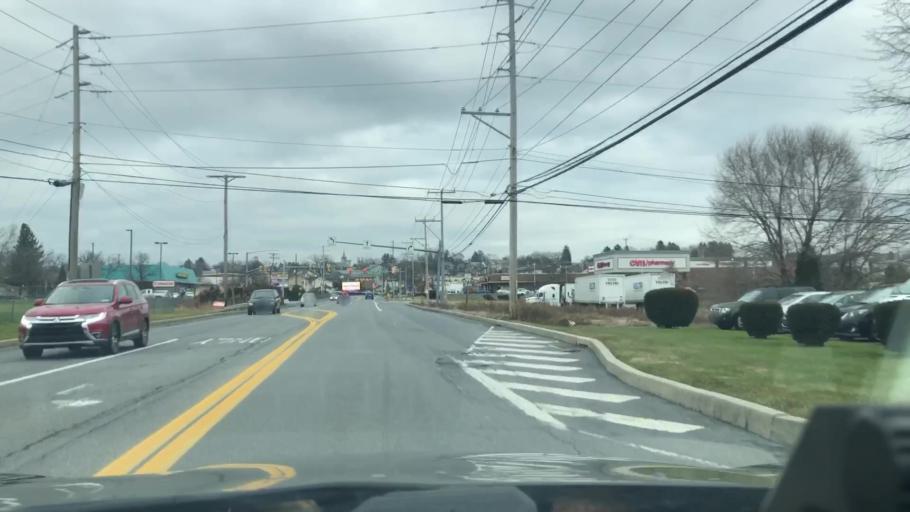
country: US
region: Pennsylvania
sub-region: Northampton County
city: Nazareth
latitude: 40.7298
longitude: -75.3142
